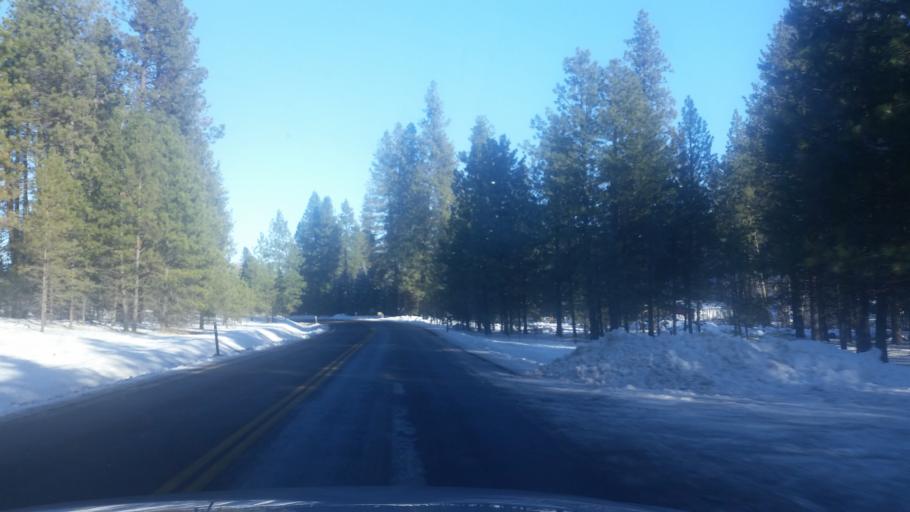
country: US
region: Washington
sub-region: Spokane County
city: Spokane
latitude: 47.5749
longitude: -117.4669
